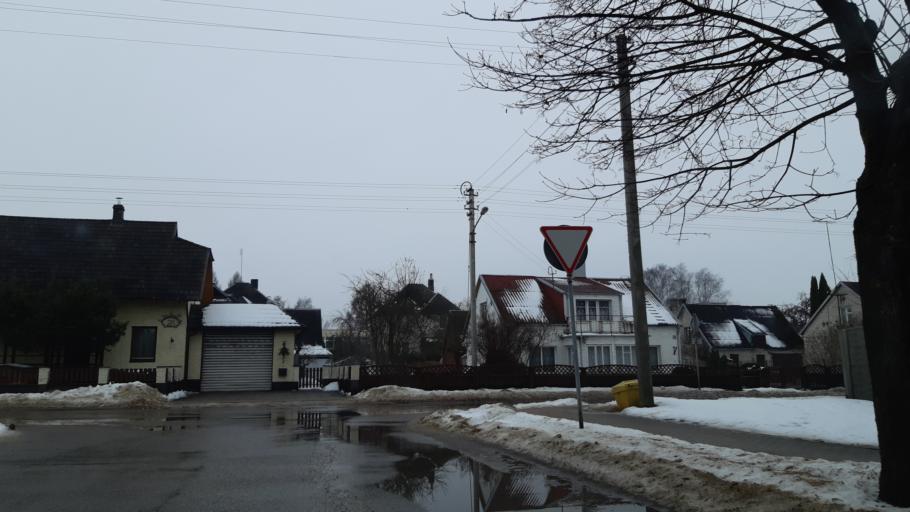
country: LT
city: Vilkaviskis
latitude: 54.6465
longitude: 23.0346
